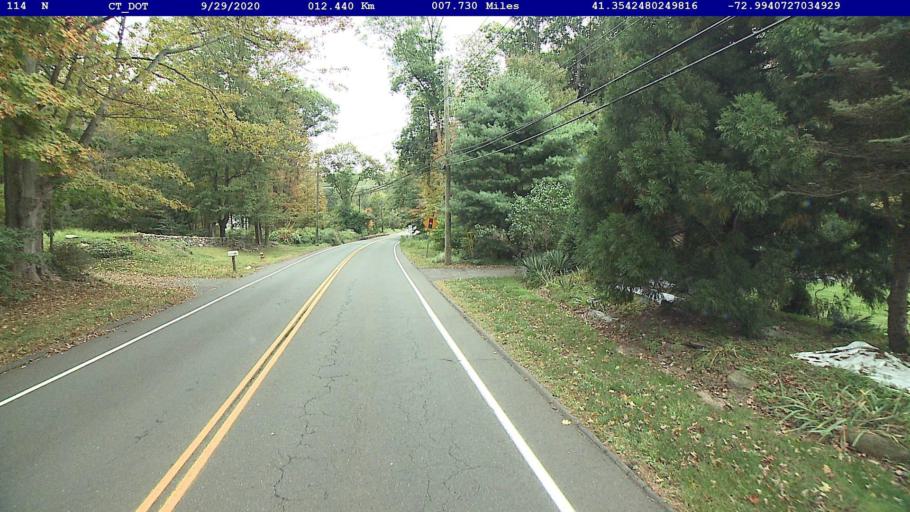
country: US
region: Connecticut
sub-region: New Haven County
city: Woodbridge
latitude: 41.3537
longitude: -72.9933
